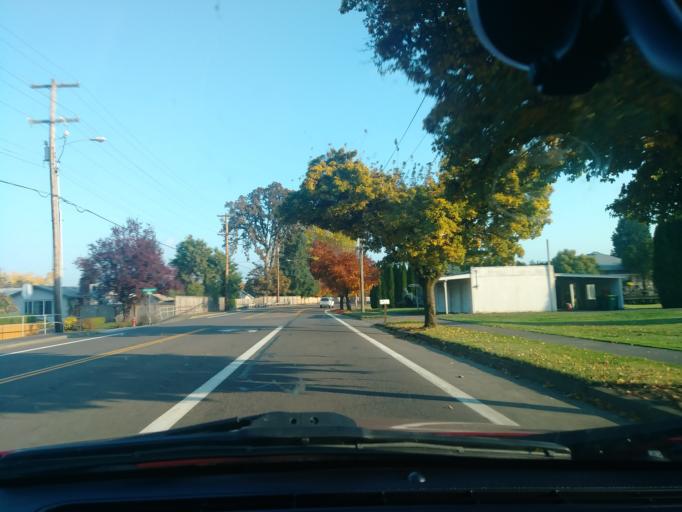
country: US
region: Oregon
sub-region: Washington County
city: Forest Grove
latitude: 45.5293
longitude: -123.1243
